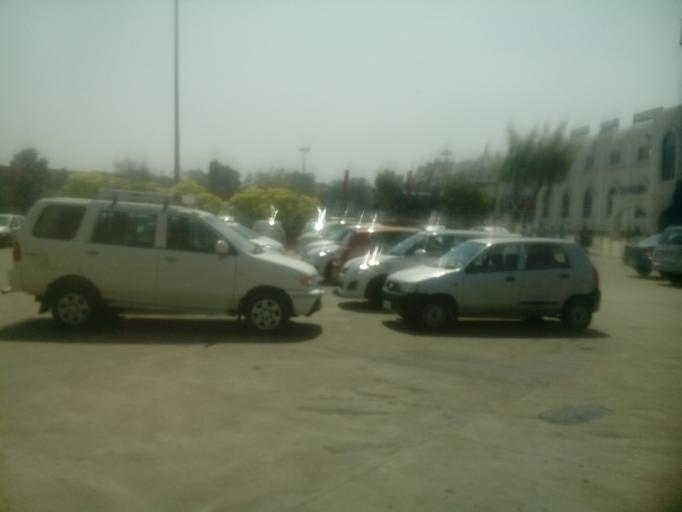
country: IN
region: Andhra Pradesh
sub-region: Krishna
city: Vijayawada
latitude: 16.5184
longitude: 80.6203
